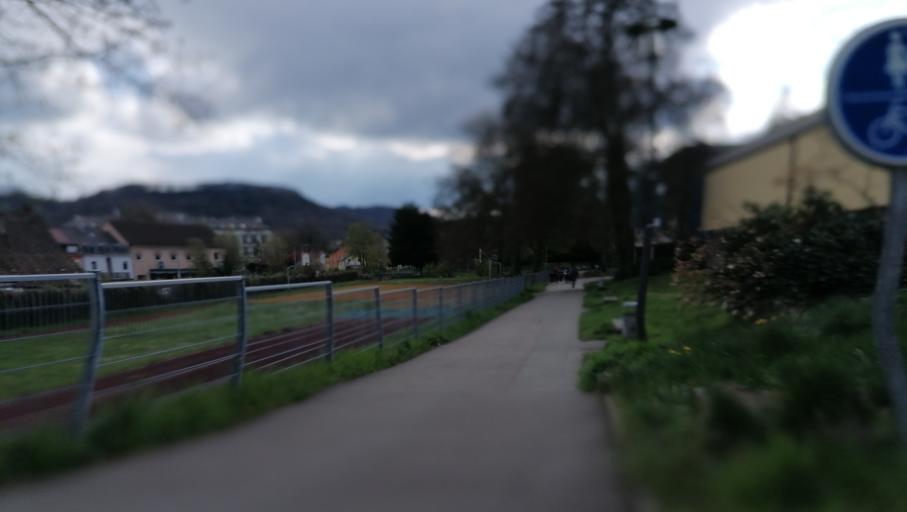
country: DE
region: Baden-Wuerttemberg
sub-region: Freiburg Region
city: Bad Sackingen
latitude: 47.5550
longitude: 7.9460
